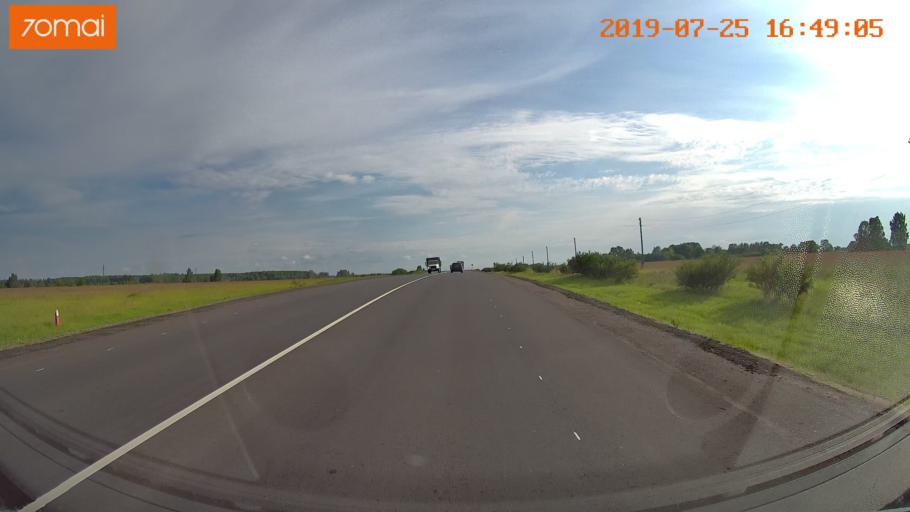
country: RU
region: Ivanovo
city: Privolzhsk
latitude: 57.3472
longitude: 41.2524
